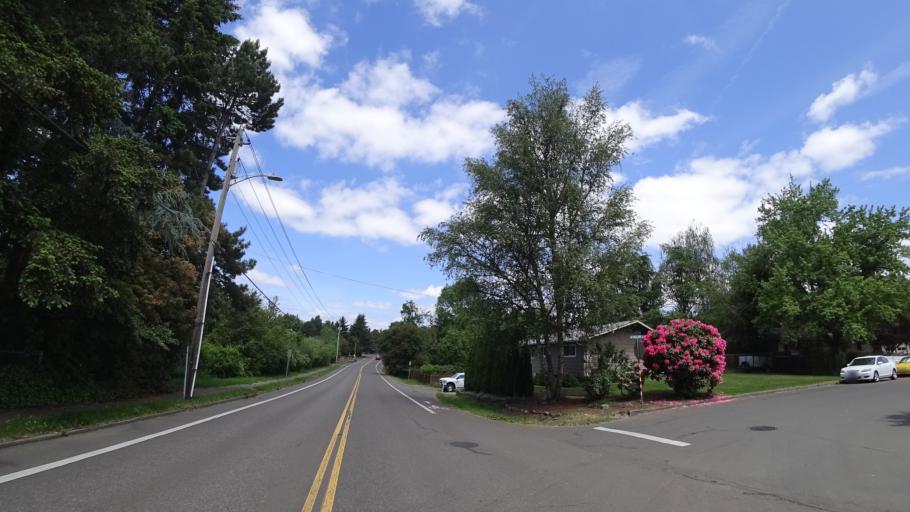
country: US
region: Oregon
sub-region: Washington County
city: Tigard
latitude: 45.4339
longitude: -122.8000
